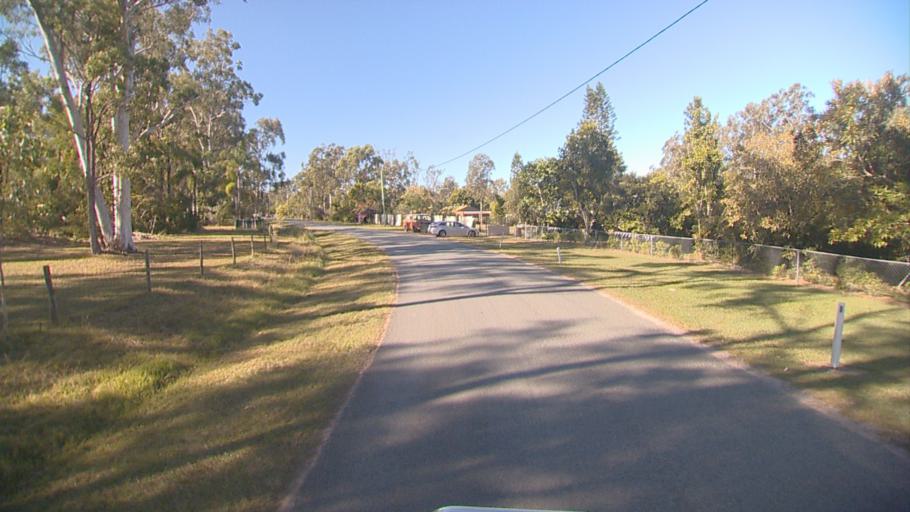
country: AU
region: Queensland
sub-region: Logan
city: Chambers Flat
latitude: -27.7369
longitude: 153.0652
